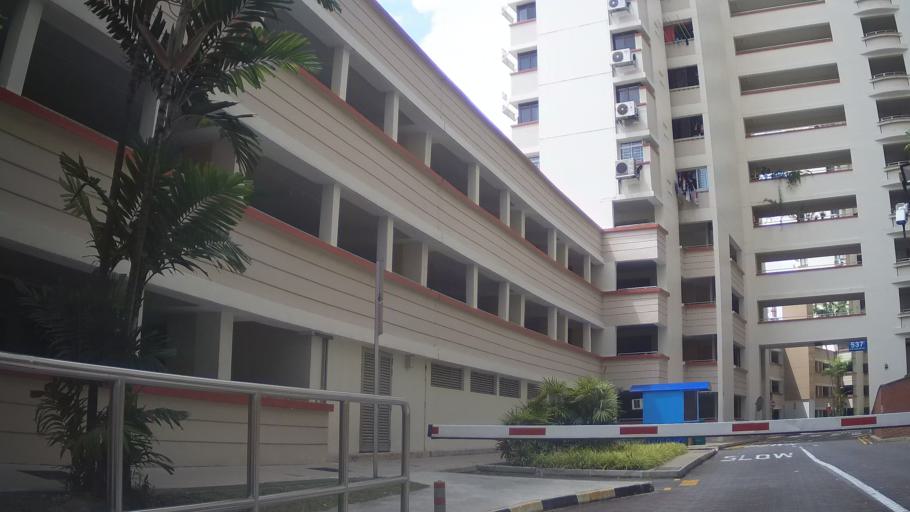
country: MY
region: Johor
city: Johor Bahru
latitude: 1.3836
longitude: 103.7631
